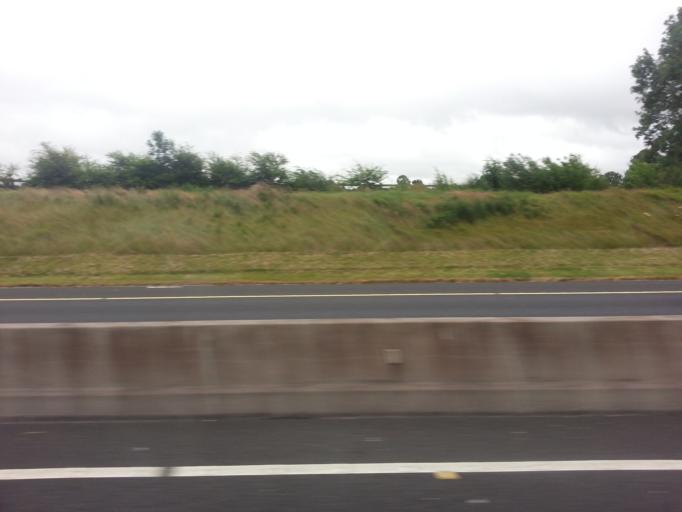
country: IE
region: Leinster
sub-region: Kildare
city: Castledermot
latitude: 52.9250
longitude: -6.8666
